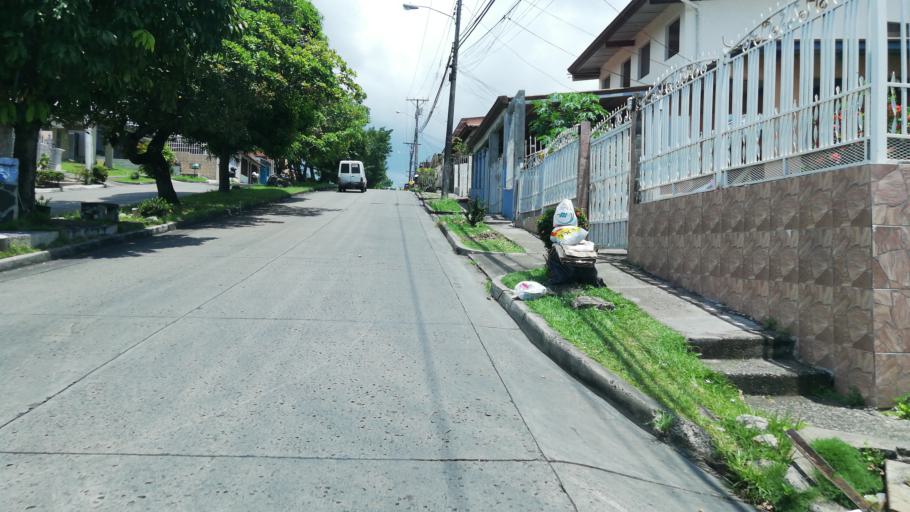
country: PA
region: Panama
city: San Miguelito
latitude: 9.0543
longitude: -79.4548
